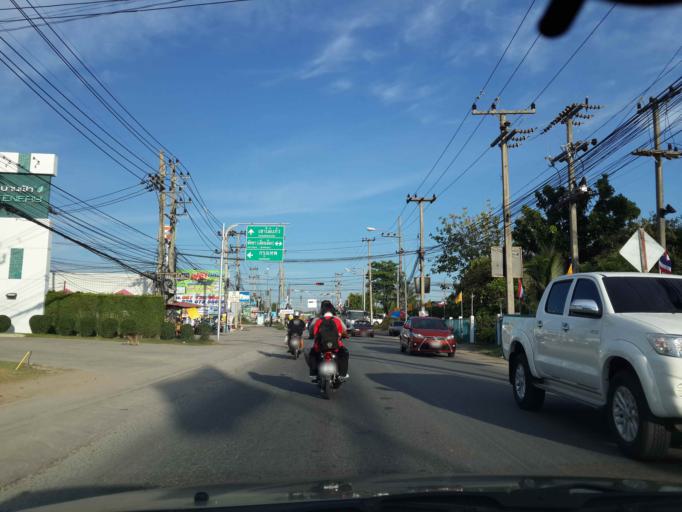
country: TH
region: Chon Buri
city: Phatthaya
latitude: 12.9636
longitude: 100.9198
